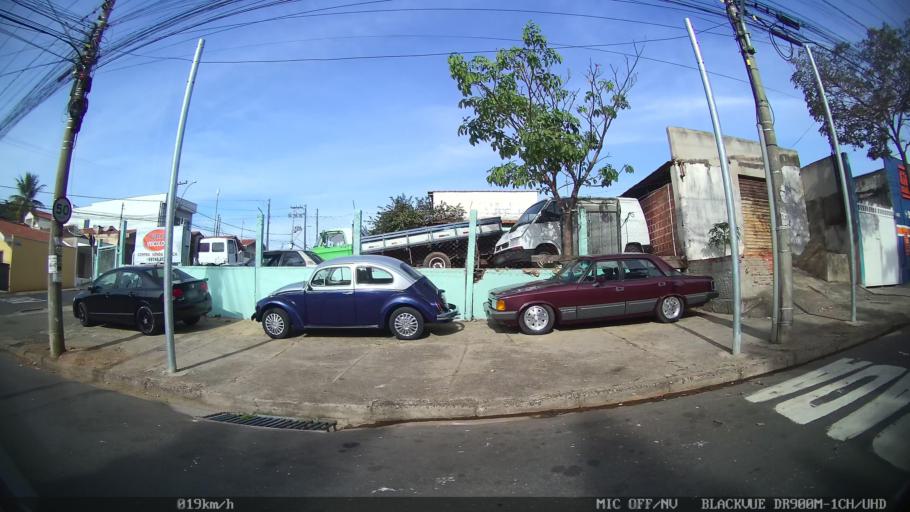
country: BR
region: Sao Paulo
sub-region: Piracicaba
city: Piracicaba
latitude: -22.7443
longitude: -47.6642
